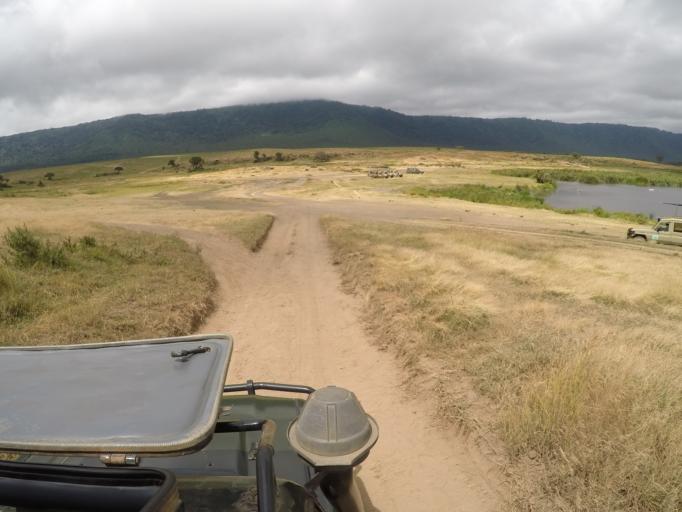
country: TZ
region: Arusha
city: Ngorongoro
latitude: -3.2101
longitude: 35.6014
